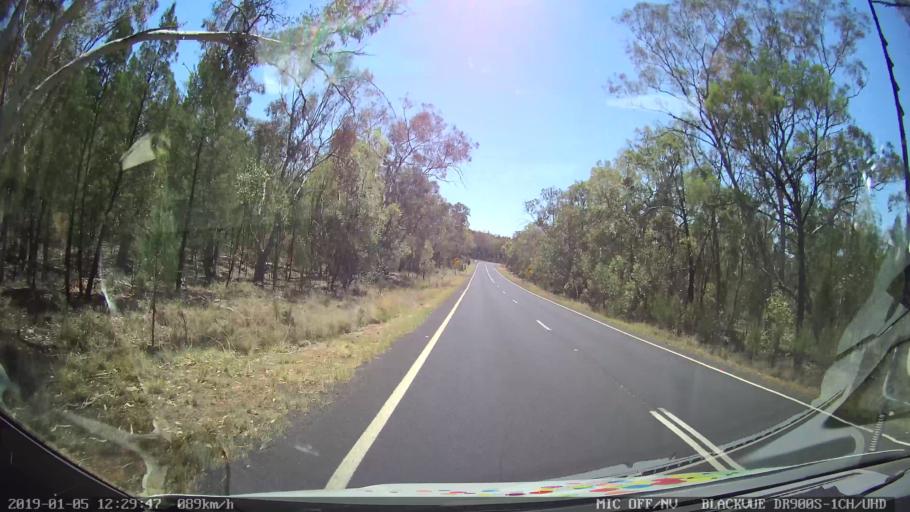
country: AU
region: New South Wales
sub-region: Warrumbungle Shire
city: Coonabarabran
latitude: -31.2310
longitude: 149.3415
